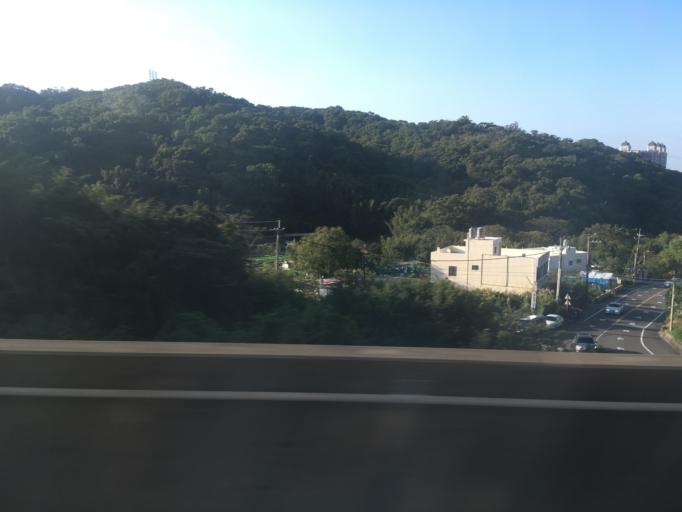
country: TW
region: Taiwan
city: Taoyuan City
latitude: 25.0549
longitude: 121.3112
